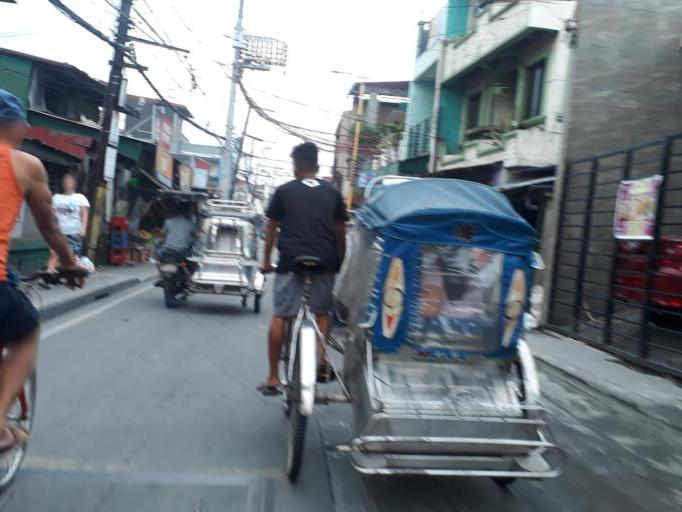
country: PH
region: Calabarzon
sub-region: Province of Rizal
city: Navotas
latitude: 14.6588
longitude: 120.9454
